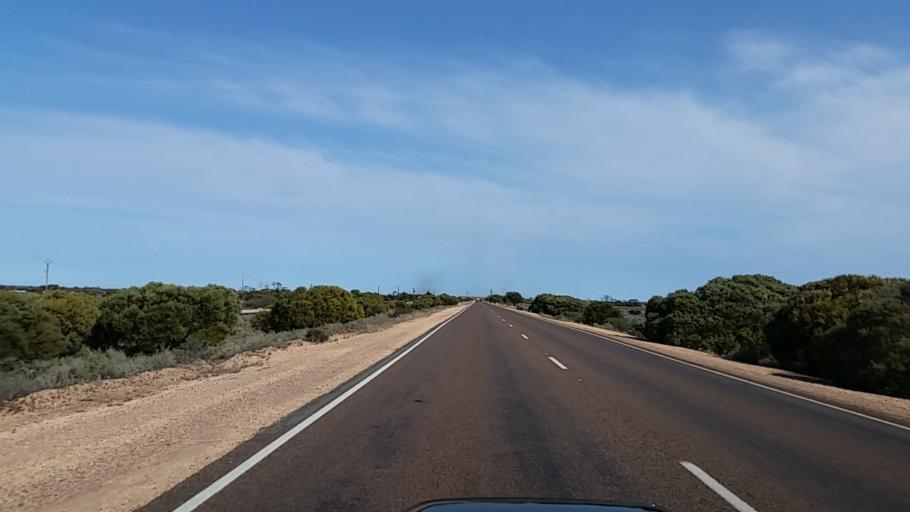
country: AU
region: South Australia
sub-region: Whyalla
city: Whyalla
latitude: -32.9623
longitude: 137.5772
